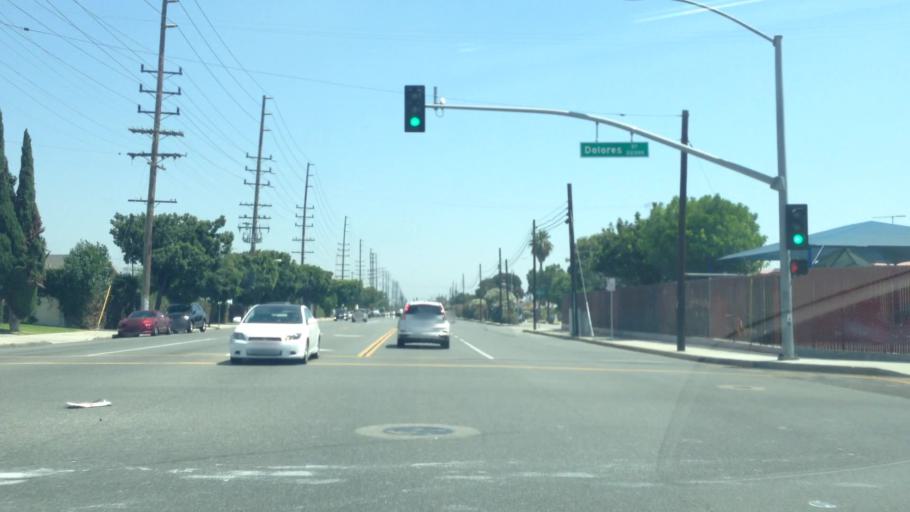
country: US
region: California
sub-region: Los Angeles County
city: Carson
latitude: 33.8242
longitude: -118.2725
